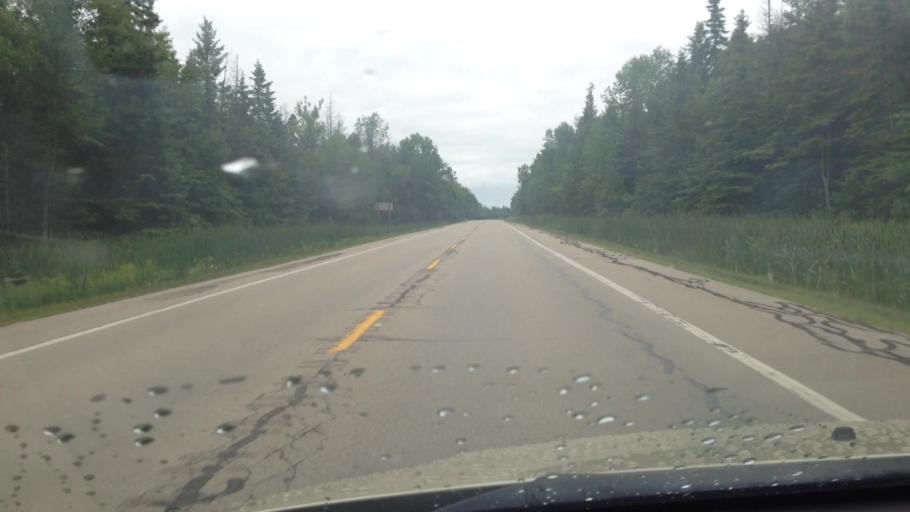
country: US
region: Michigan
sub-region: Menominee County
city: Menominee
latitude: 45.3974
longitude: -87.3662
